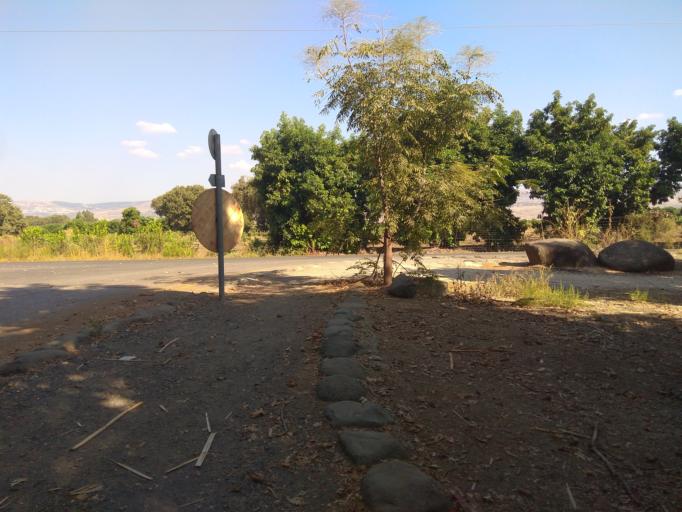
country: IL
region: Northern District
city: Qiryat Shemona
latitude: 33.2310
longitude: 35.6248
